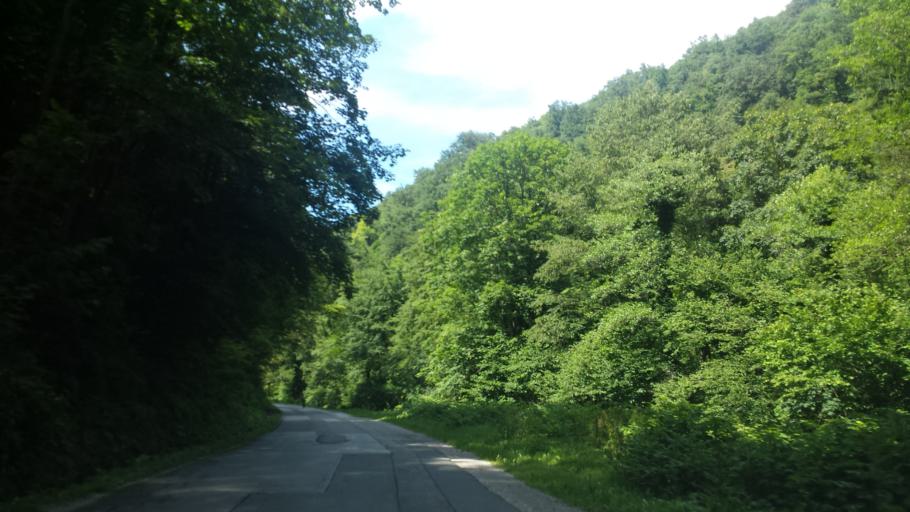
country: HR
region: Zagrebacka
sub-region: Grad Samobor
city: Samobor
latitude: 45.7919
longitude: 15.6922
